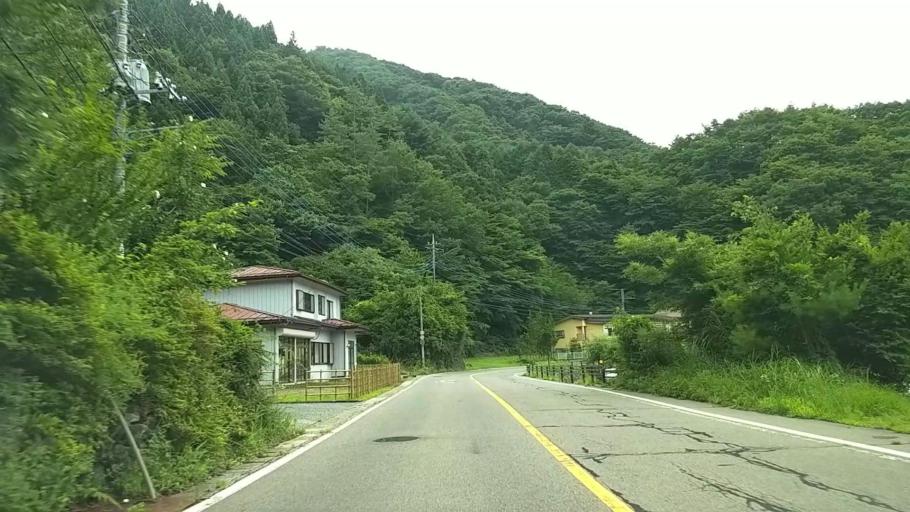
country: JP
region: Yamanashi
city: Fujikawaguchiko
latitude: 35.4970
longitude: 138.6970
